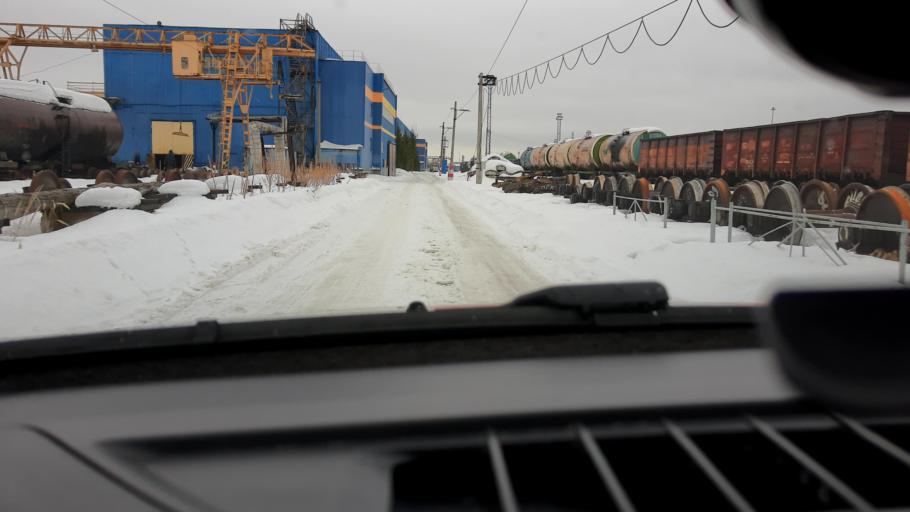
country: RU
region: Nizjnij Novgorod
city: Gorbatovka
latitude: 56.2840
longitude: 43.8553
